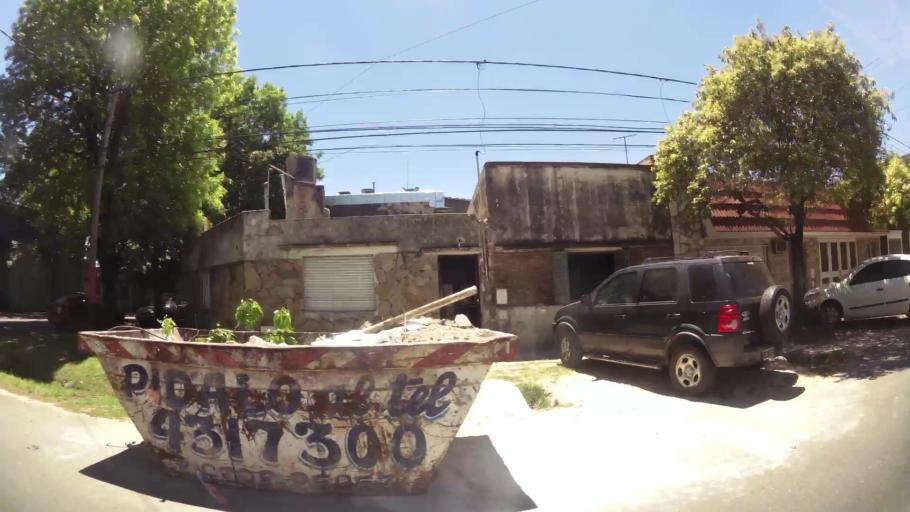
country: AR
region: Santa Fe
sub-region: Departamento de Rosario
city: Rosario
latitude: -32.9507
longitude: -60.6847
